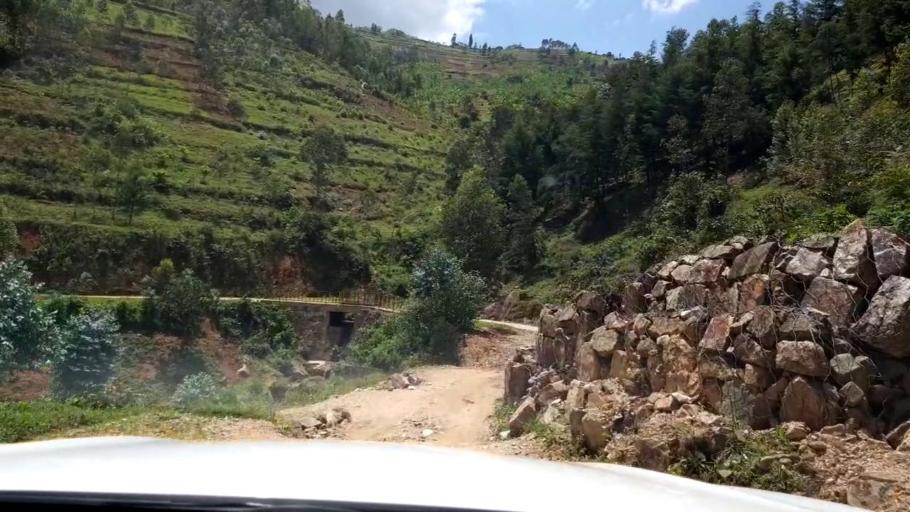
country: RW
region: Southern Province
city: Gitarama
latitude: -1.9856
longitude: 29.6215
